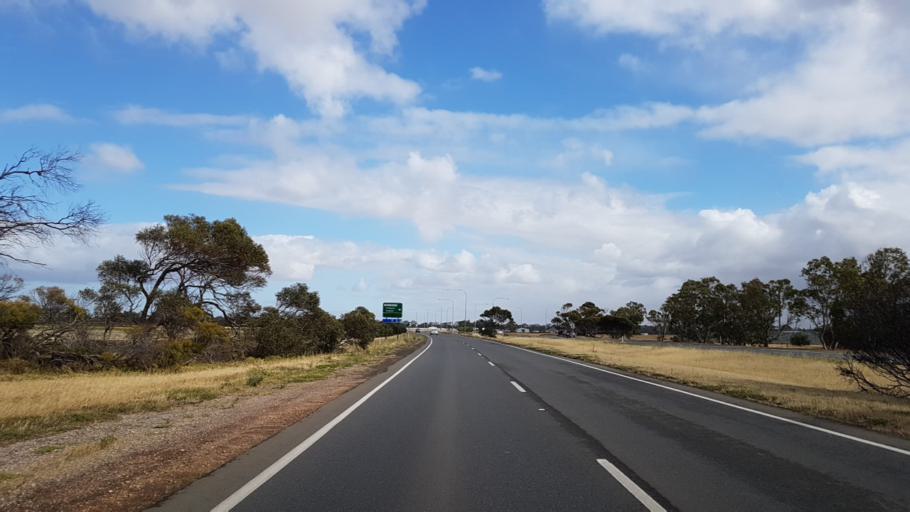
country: AU
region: South Australia
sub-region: Playford
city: Virginia
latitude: -34.6544
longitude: 138.5424
